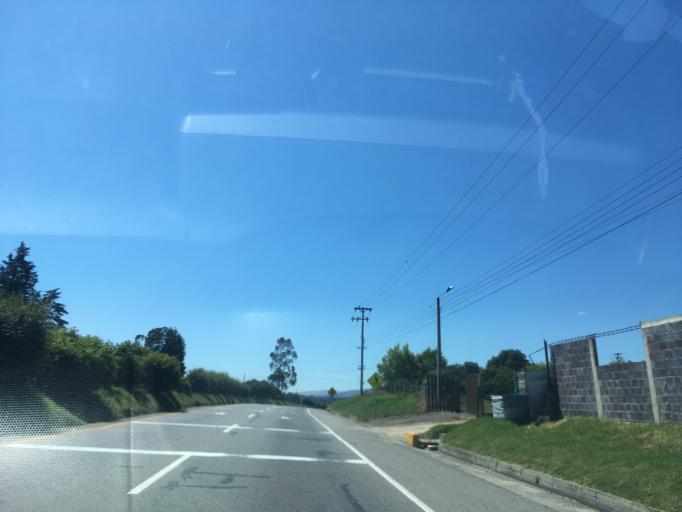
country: CO
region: Boyaca
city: Tuta
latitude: 5.7166
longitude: -73.2292
